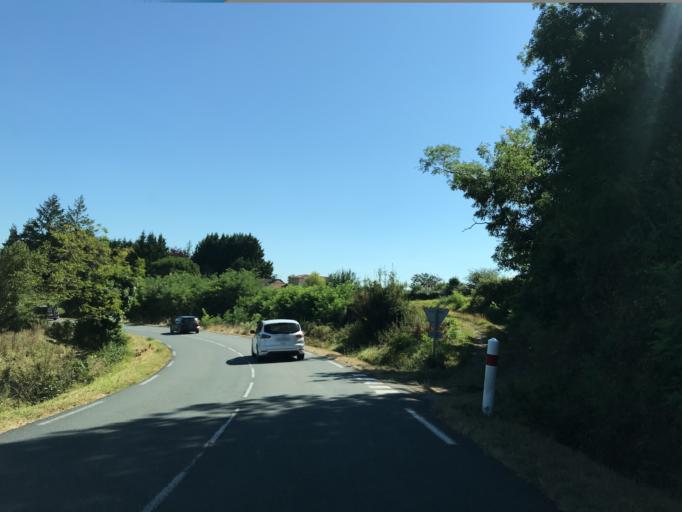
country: FR
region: Limousin
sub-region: Departement de la Correze
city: Larche
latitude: 45.1115
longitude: 1.3956
